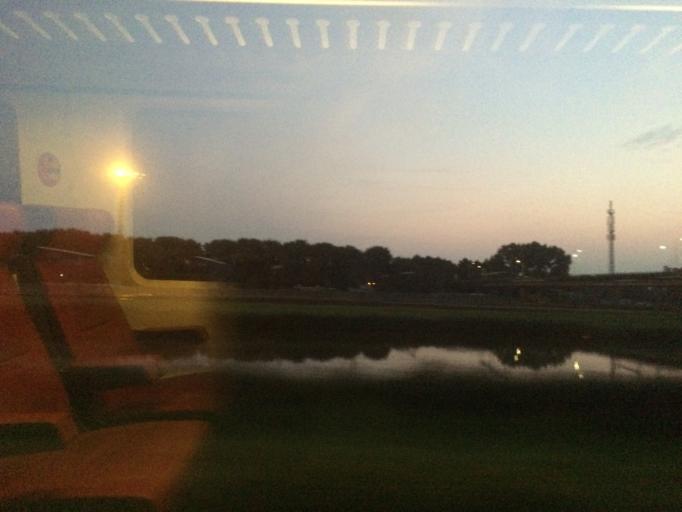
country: NL
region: South Holland
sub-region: Gemeente Zwijndrecht
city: Zwijndrecht
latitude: 51.8282
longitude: 4.6097
